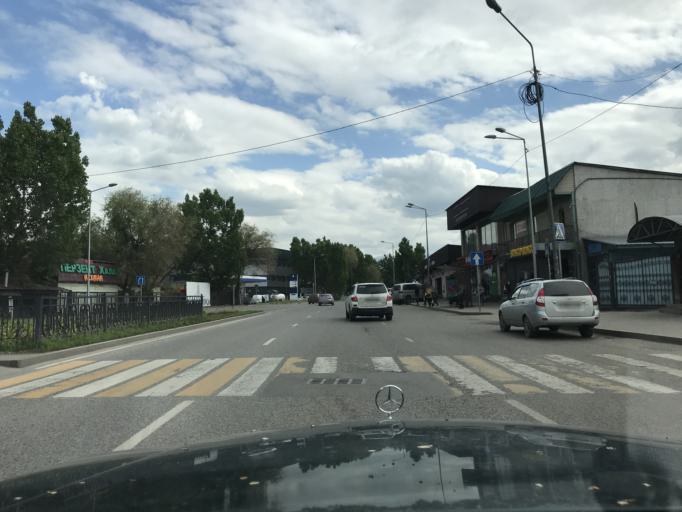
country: KZ
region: Almaty Qalasy
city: Almaty
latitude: 43.3015
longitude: 76.8972
